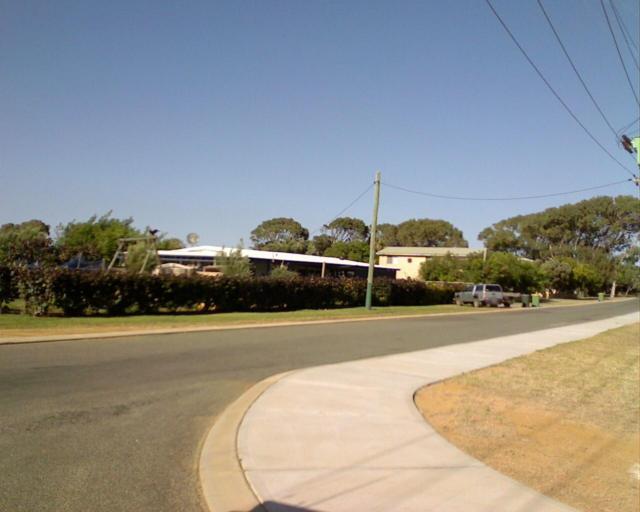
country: AU
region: Western Australia
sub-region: Dandaragan
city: Jurien Bay
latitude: -30.0637
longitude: 114.9687
